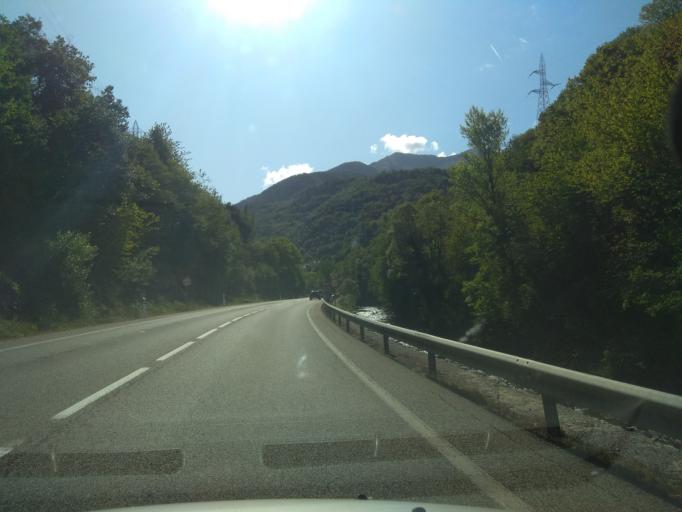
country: ES
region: Catalonia
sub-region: Provincia de Lleida
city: Les
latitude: 42.7383
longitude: 0.7282
